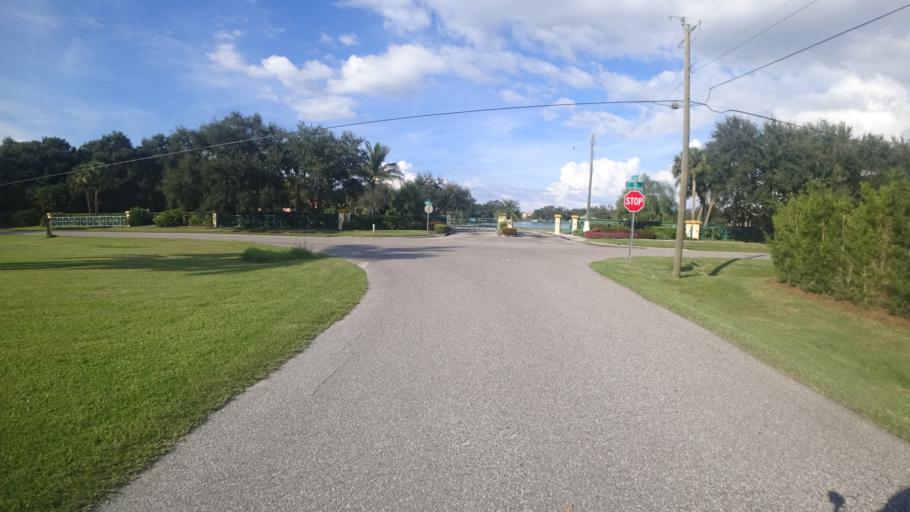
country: US
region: Florida
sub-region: Manatee County
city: West Bradenton
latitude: 27.5297
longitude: -82.6159
